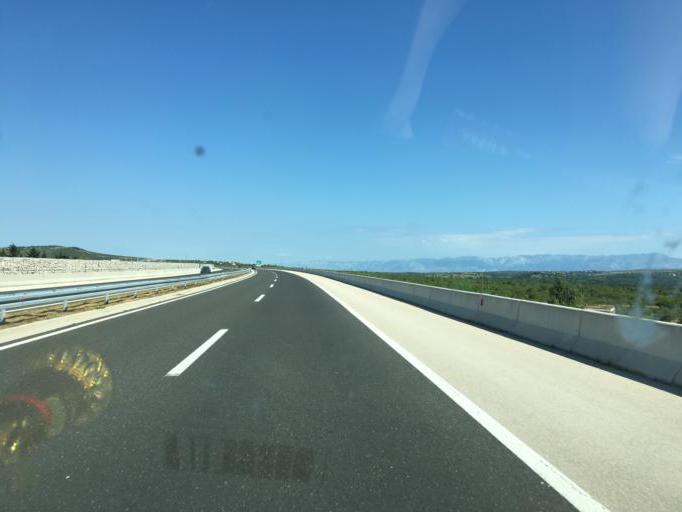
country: HR
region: Zadarska
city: Polaca
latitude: 44.0515
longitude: 15.5445
